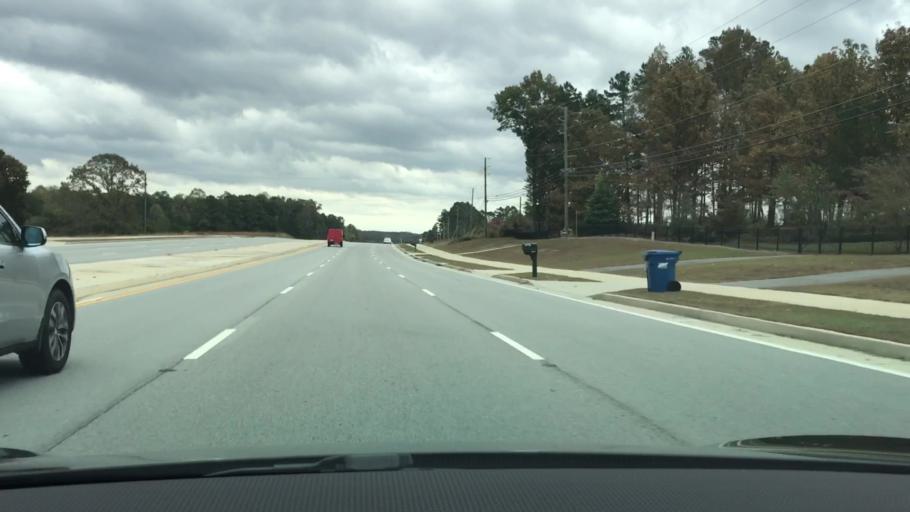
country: US
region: Georgia
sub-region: Hall County
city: Flowery Branch
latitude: 34.1164
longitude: -83.9077
